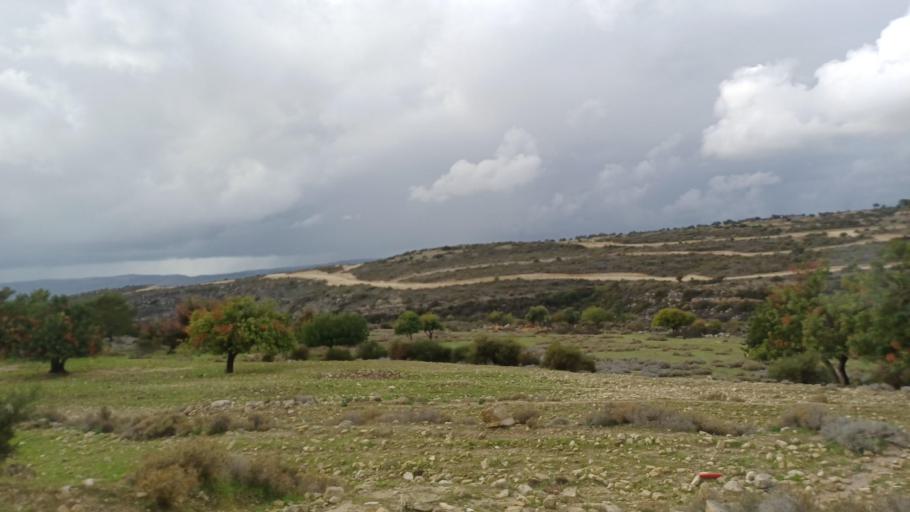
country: CY
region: Limassol
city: Sotira
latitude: 34.7262
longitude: 32.8191
